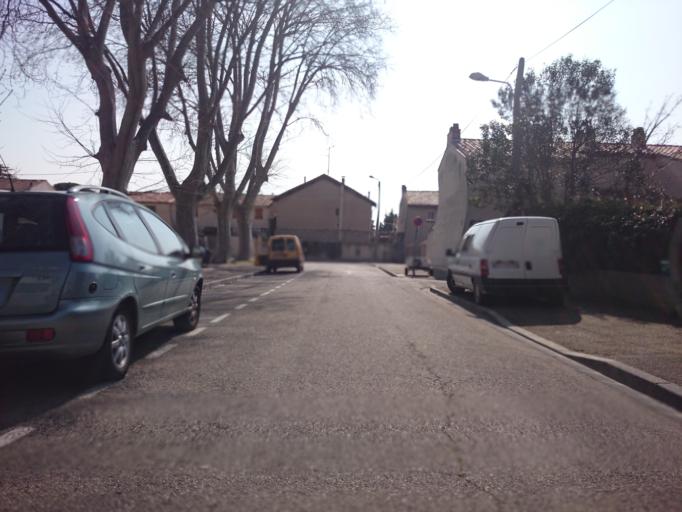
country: FR
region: Provence-Alpes-Cote d'Azur
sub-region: Departement du Vaucluse
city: Avignon
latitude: 43.9379
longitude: 4.8187
